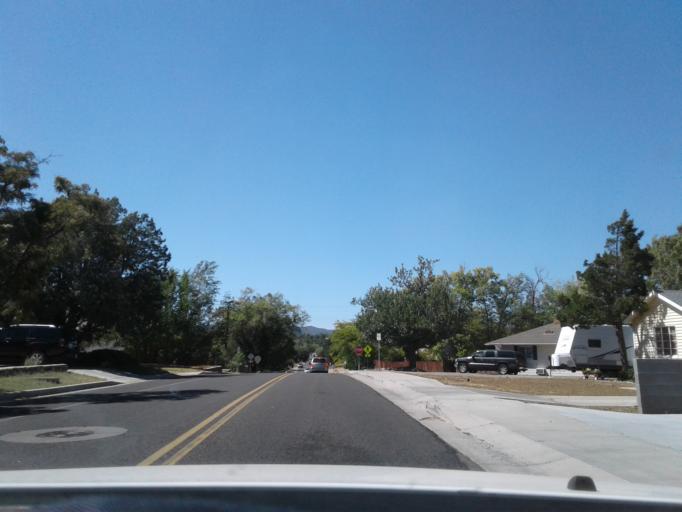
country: US
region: Arizona
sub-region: Yavapai County
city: Prescott
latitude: 34.5709
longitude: -112.4758
